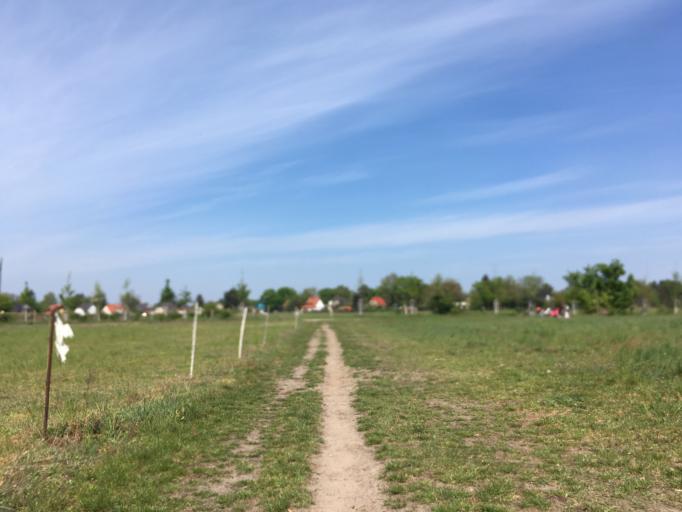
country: DE
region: Berlin
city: Blankenfelde
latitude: 52.6399
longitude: 13.3809
